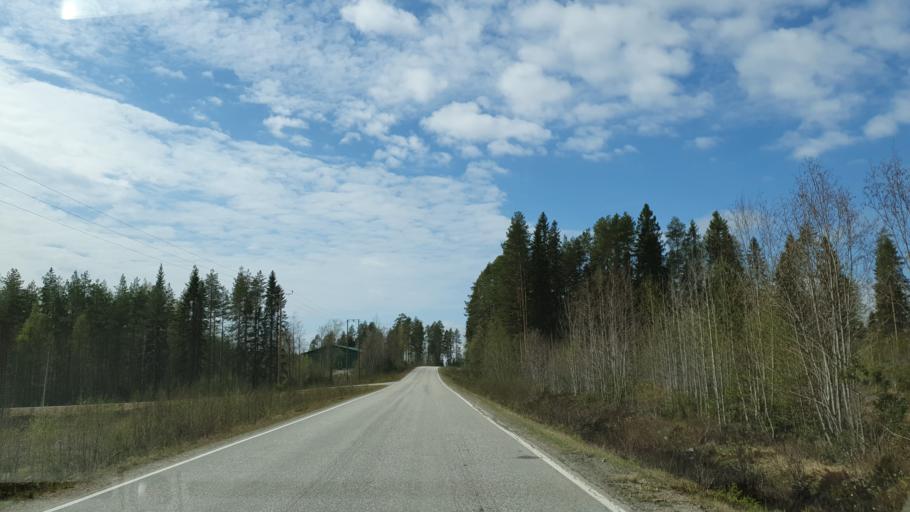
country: FI
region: Kainuu
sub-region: Kehys-Kainuu
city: Kuhmo
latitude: 64.1215
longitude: 29.6730
